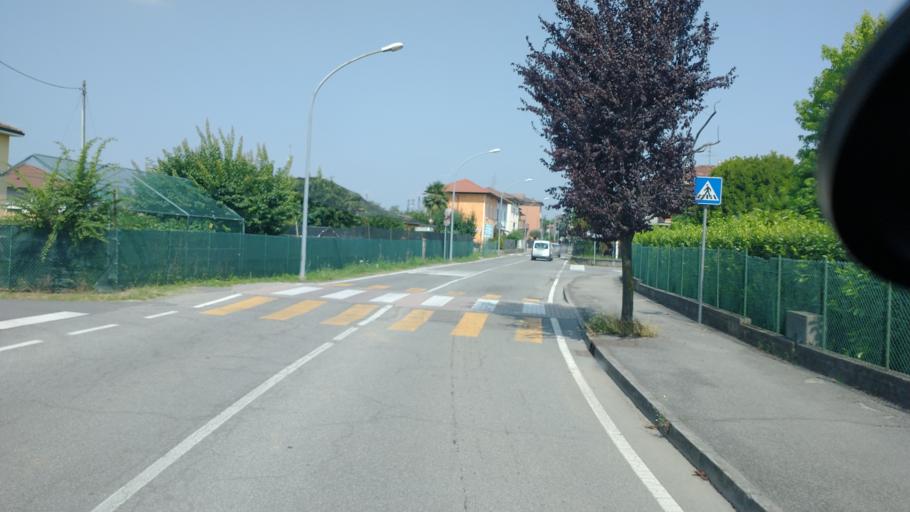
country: IT
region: Lombardy
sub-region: Provincia di Bergamo
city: Levate
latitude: 45.6360
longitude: 9.6183
